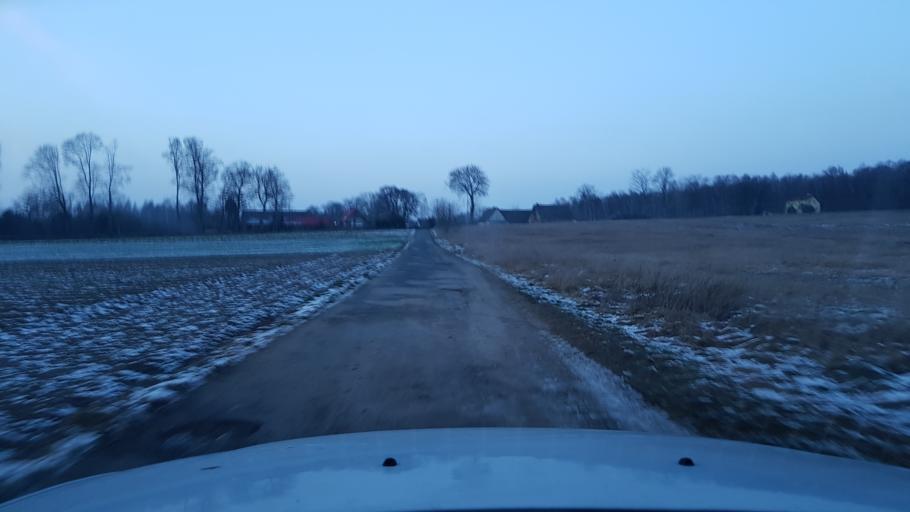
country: PL
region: West Pomeranian Voivodeship
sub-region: Powiat swidwinski
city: Slawoborze
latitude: 53.9675
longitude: 15.7648
